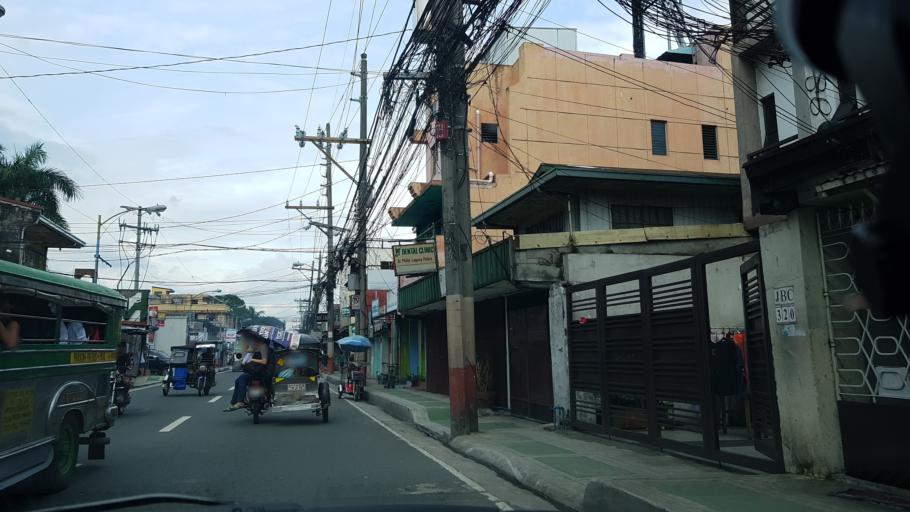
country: PH
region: Metro Manila
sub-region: Pasig
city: Pasig City
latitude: 14.5726
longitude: 121.0780
